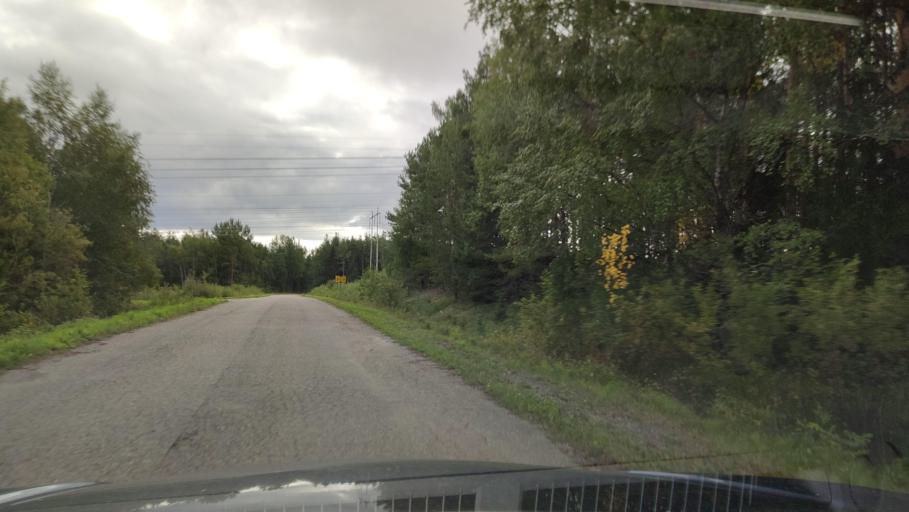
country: FI
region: Ostrobothnia
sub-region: Sydosterbotten
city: Kristinestad
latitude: 62.2562
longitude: 21.3355
